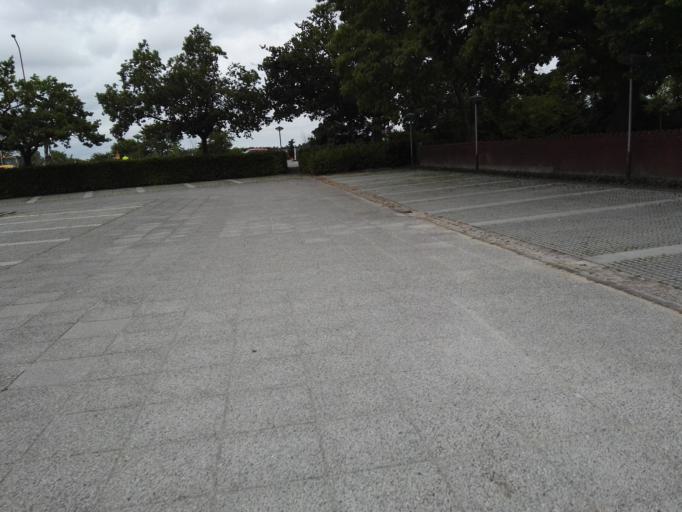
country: DK
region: Capital Region
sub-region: Ballerup Kommune
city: Ballerup
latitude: 55.7390
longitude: 12.3648
